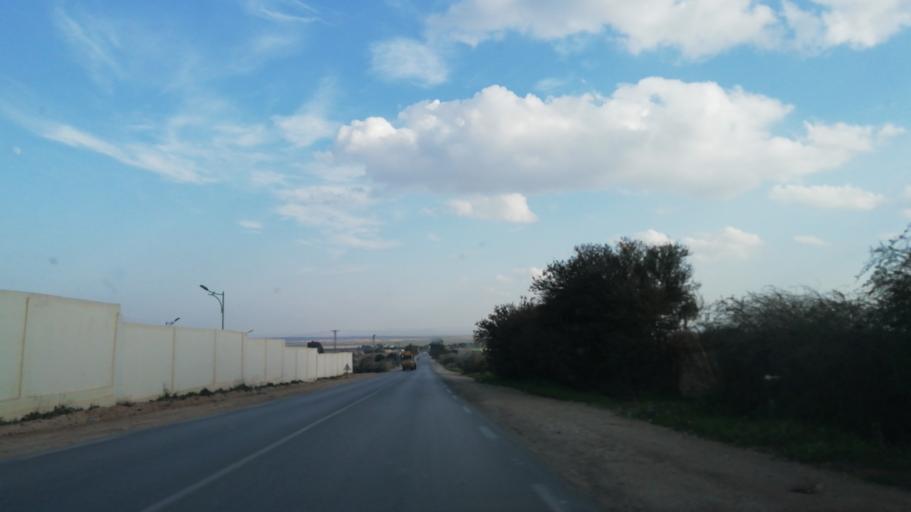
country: DZ
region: Relizane
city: Relizane
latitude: 35.9045
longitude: 0.5161
